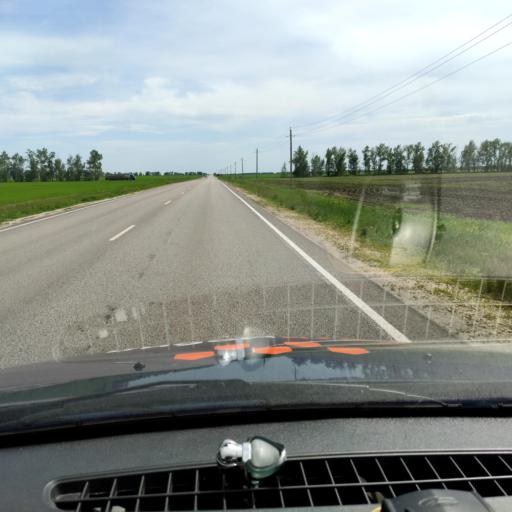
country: RU
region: Voronezj
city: Novaya Usman'
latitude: 51.5673
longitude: 39.3756
